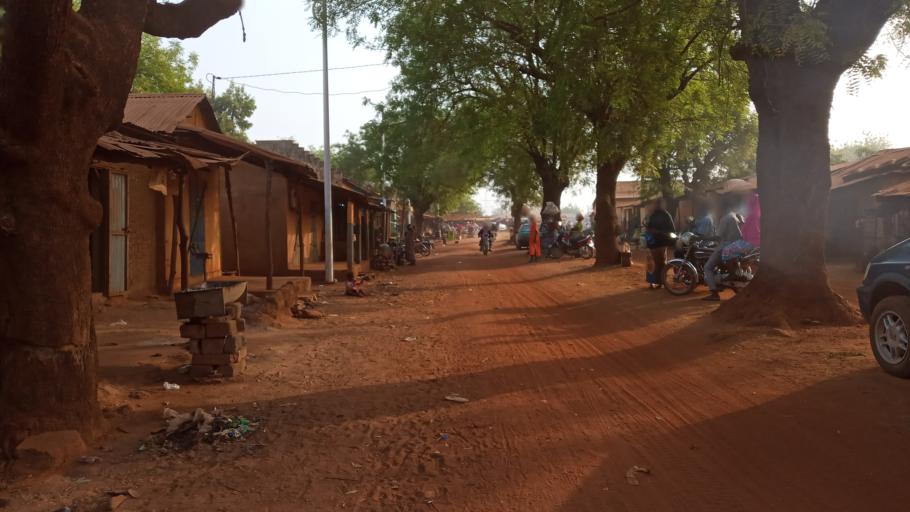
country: TG
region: Savanes
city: Sansanne-Mango
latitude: 10.3556
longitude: 0.4746
